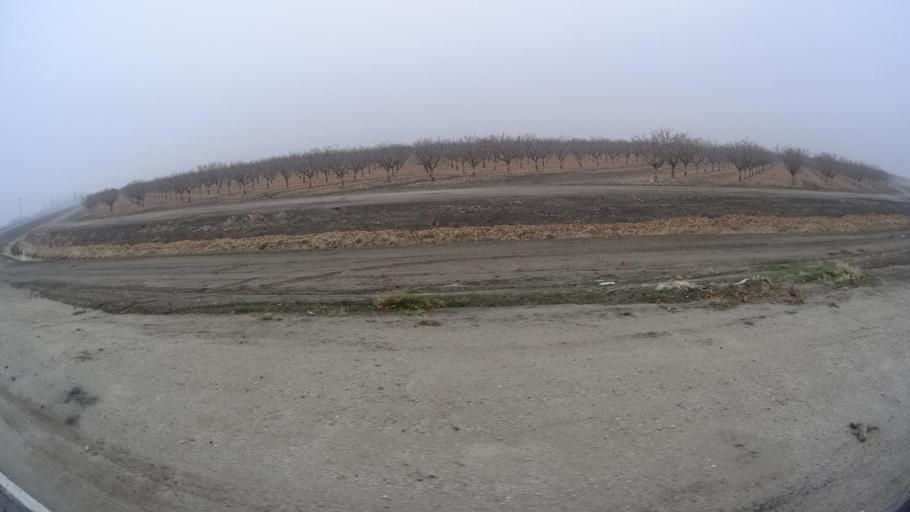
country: US
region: California
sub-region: Kern County
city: Buttonwillow
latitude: 35.4198
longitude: -119.5189
